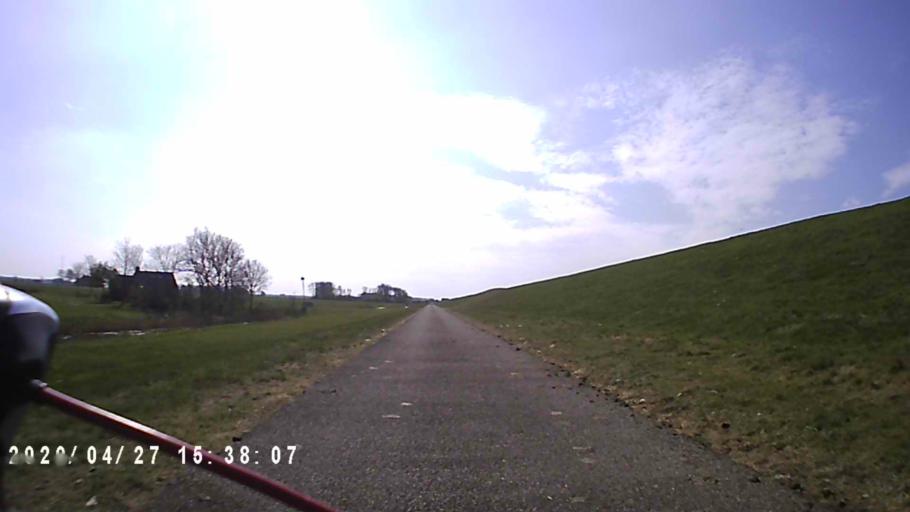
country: NL
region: Groningen
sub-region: Gemeente De Marne
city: Ulrum
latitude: 53.3953
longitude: 6.3202
